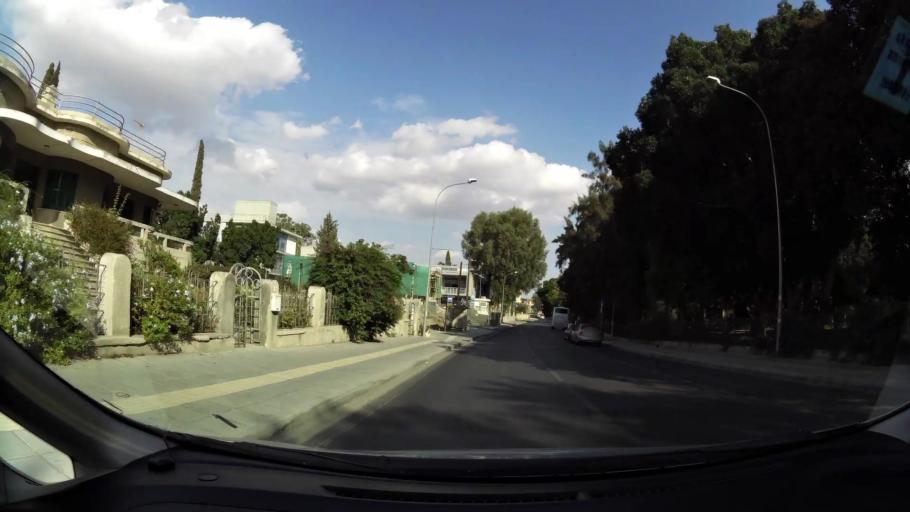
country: CY
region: Lefkosia
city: Nicosia
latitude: 35.1737
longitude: 33.3528
